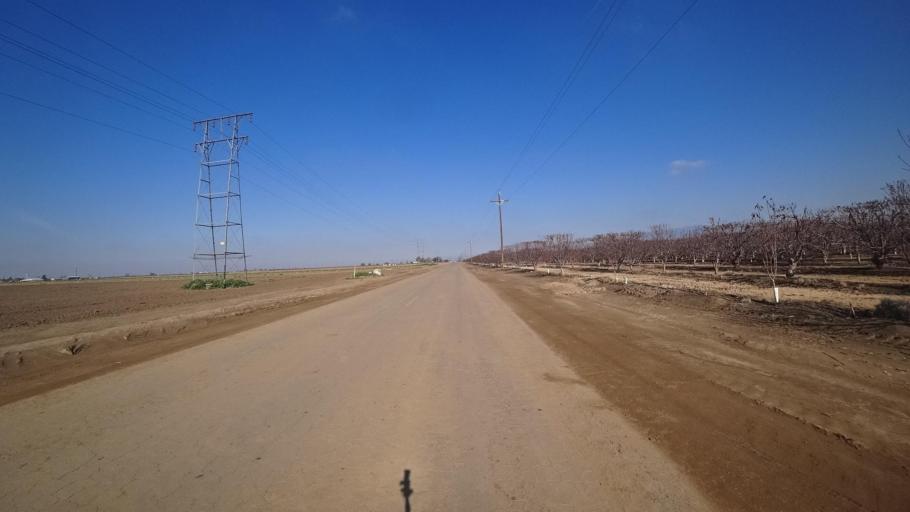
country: US
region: California
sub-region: Kern County
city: Arvin
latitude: 35.2033
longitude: -118.8063
